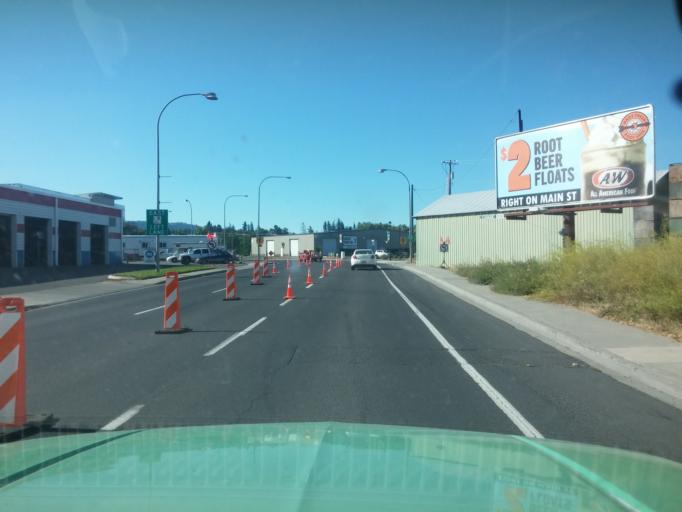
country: US
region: Idaho
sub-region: Latah County
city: Moscow
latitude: 46.7290
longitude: -117.0029
